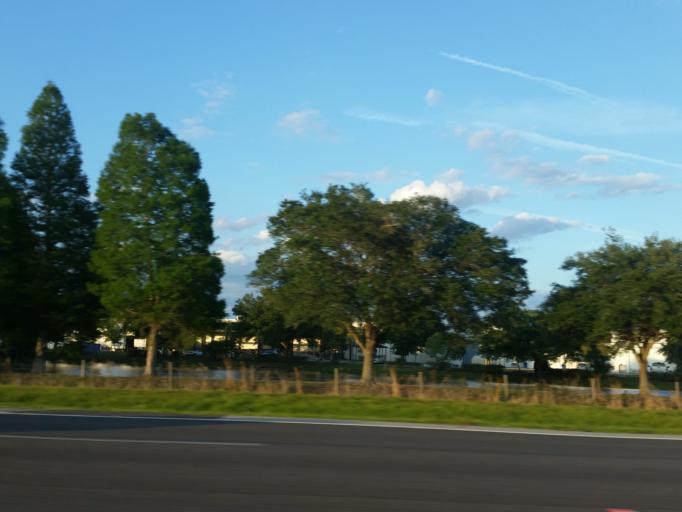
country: US
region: Florida
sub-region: Sarasota County
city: Nokomis
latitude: 27.1413
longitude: -82.4103
